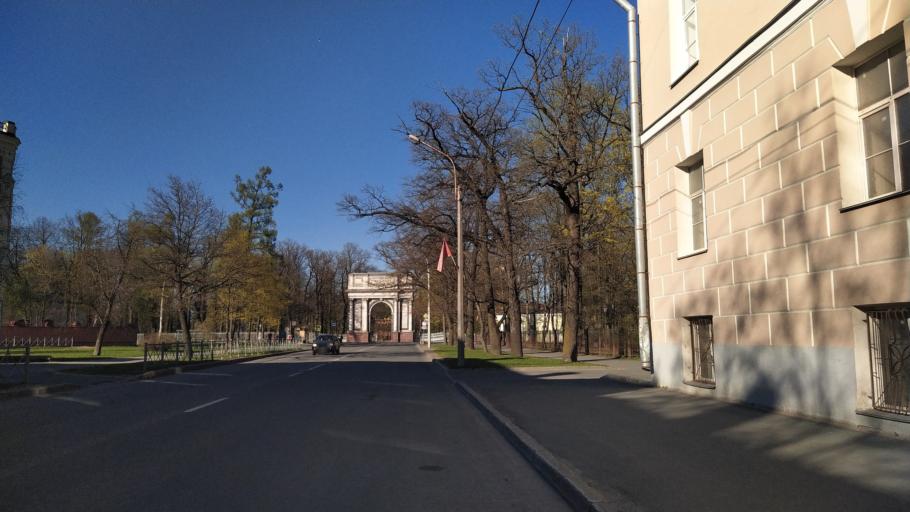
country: RU
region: St.-Petersburg
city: Pushkin
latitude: 59.7084
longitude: 30.3810
